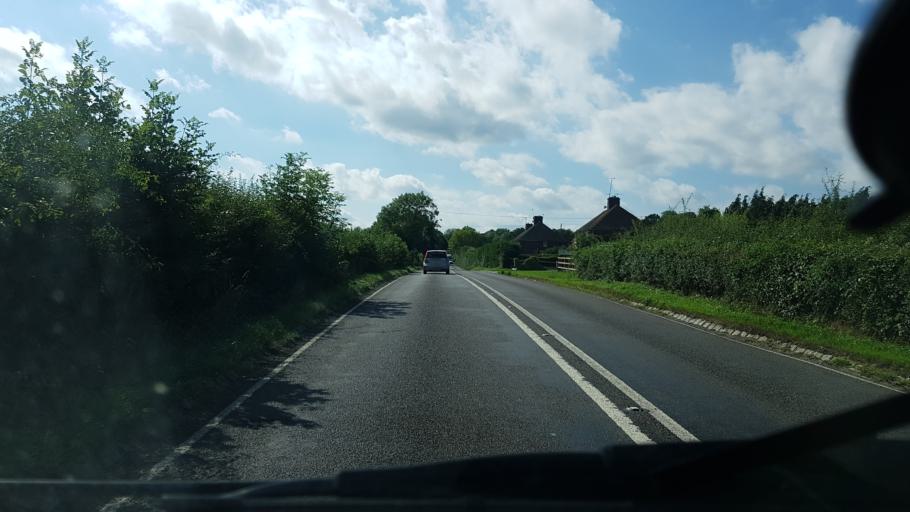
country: GB
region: England
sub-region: West Sussex
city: Rudgwick
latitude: 51.0864
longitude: -0.4305
